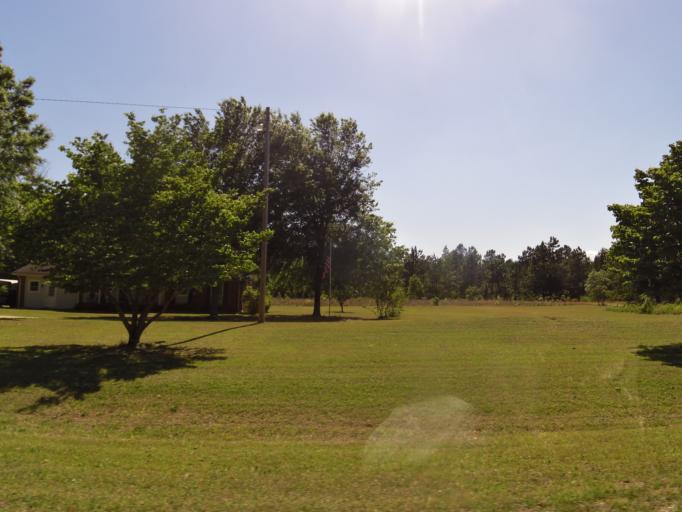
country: US
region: South Carolina
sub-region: Barnwell County
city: Williston
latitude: 33.4556
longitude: -81.4950
